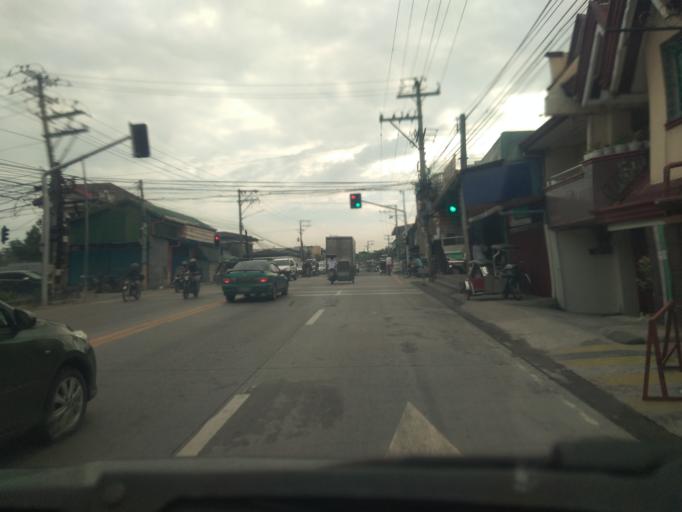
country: PH
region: Central Luzon
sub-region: Province of Pampanga
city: San Fernando
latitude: 15.0328
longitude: 120.6938
